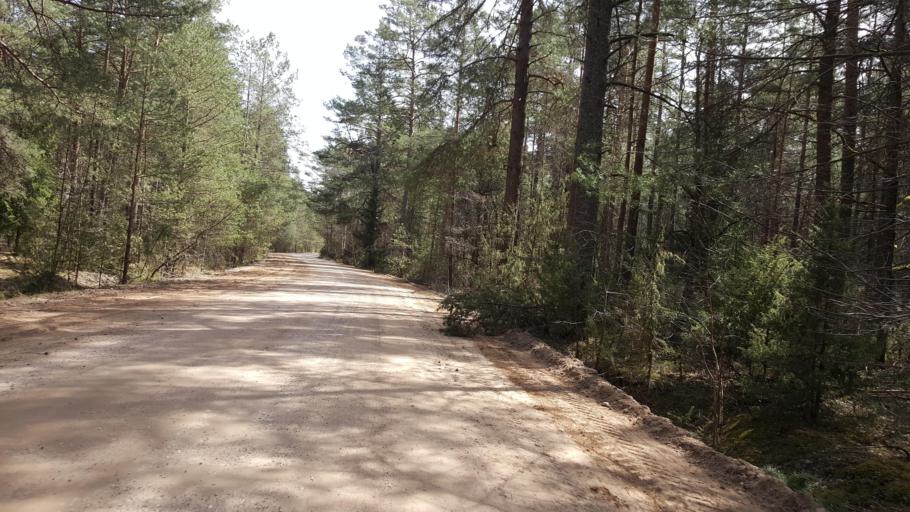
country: BY
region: Brest
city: Kamyanyuki
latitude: 52.5715
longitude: 23.7482
